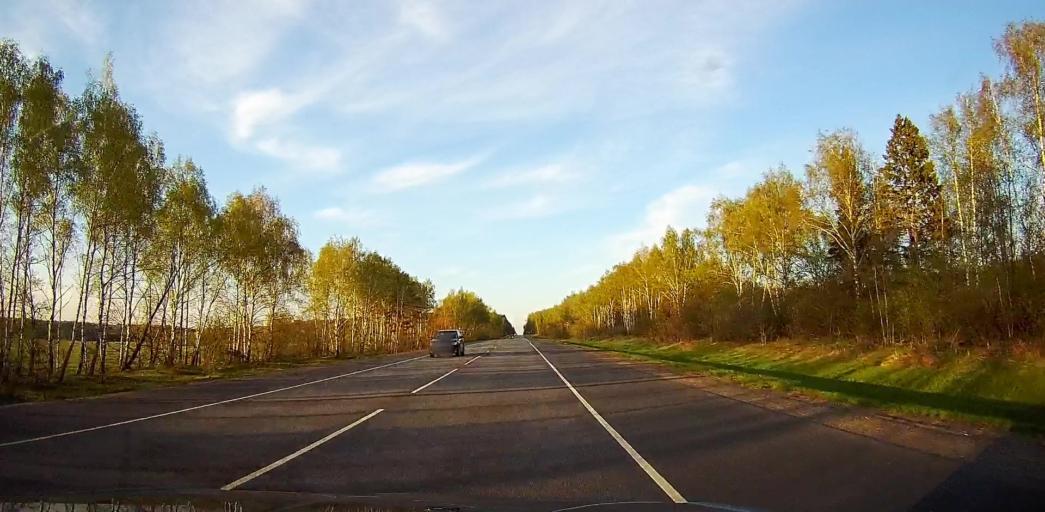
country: RU
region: Moskovskaya
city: Meshcherino
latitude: 55.2446
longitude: 38.4358
